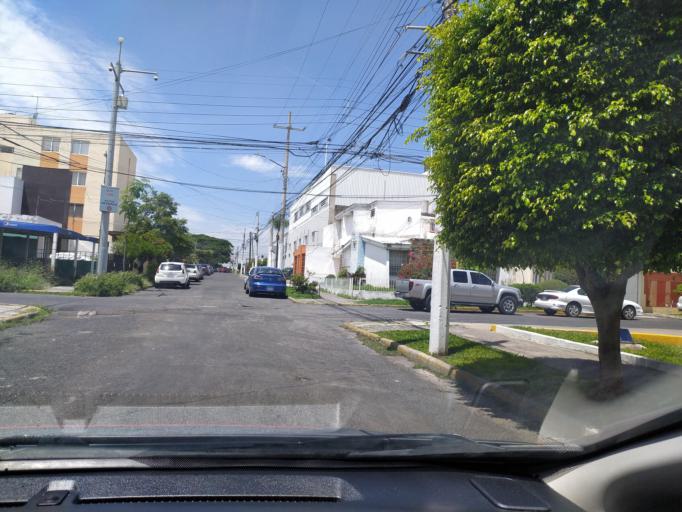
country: MX
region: Jalisco
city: Guadalajara
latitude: 20.6262
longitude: -103.4186
